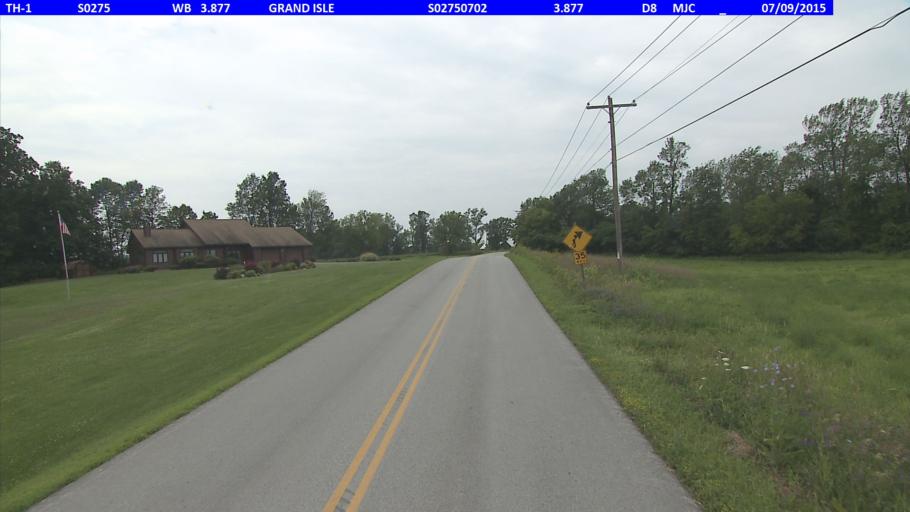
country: US
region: Vermont
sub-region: Grand Isle County
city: North Hero
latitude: 44.7372
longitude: -73.3040
